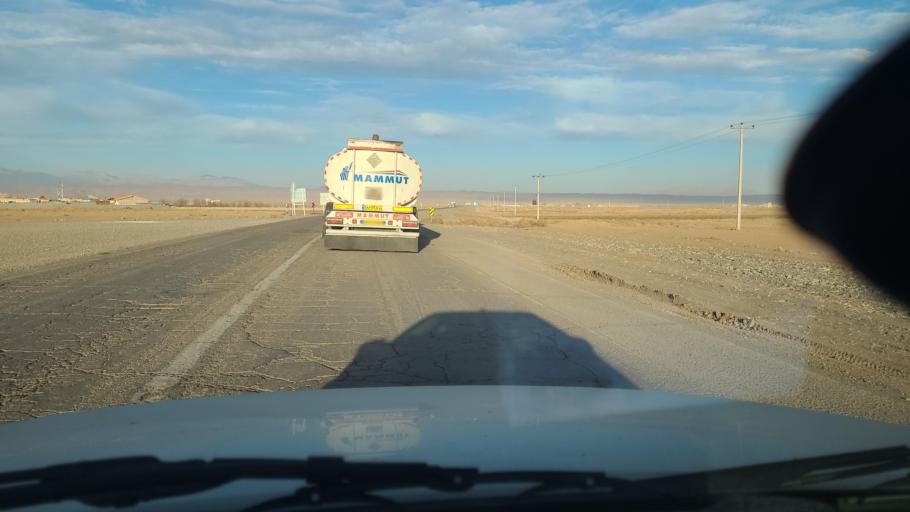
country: IR
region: Razavi Khorasan
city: Neqab
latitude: 36.6132
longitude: 57.5956
